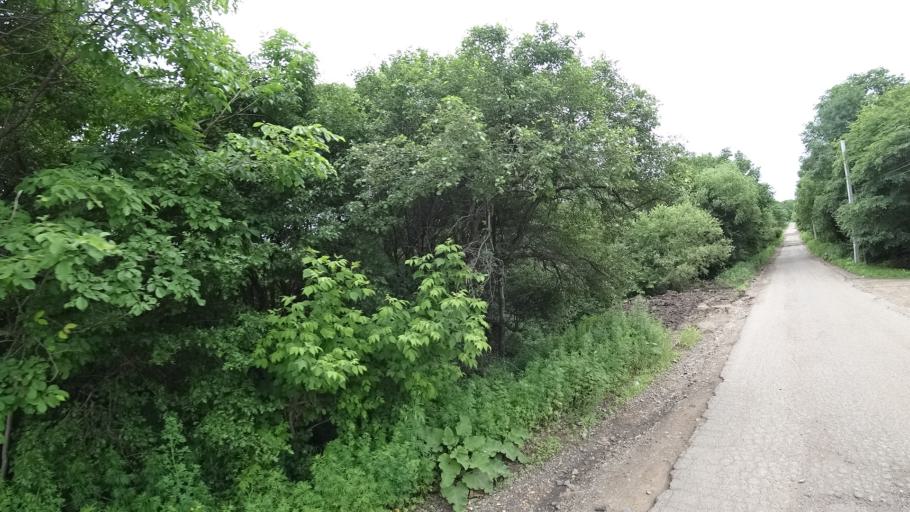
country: RU
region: Primorskiy
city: Novosysoyevka
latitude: 44.2057
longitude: 133.3280
